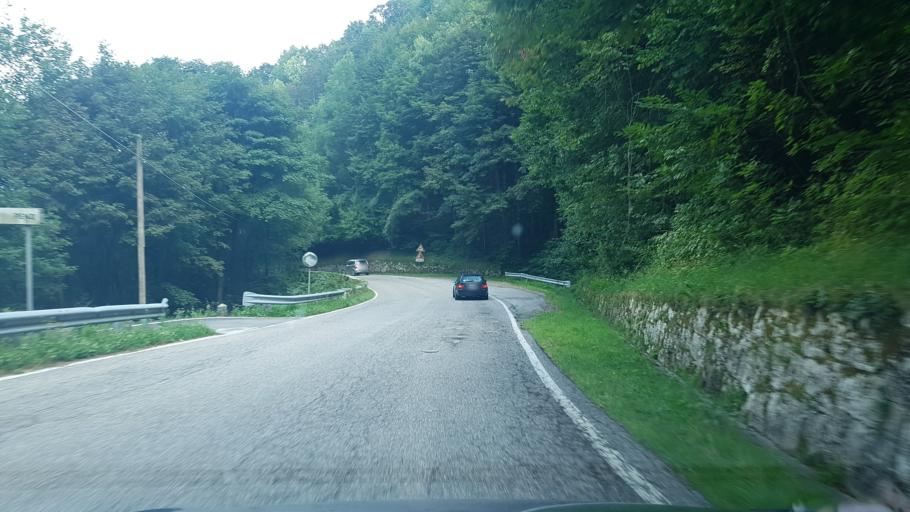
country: IT
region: Veneto
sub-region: Provincia di Vicenza
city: Recoaro Terme
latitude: 45.7593
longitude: 11.2080
